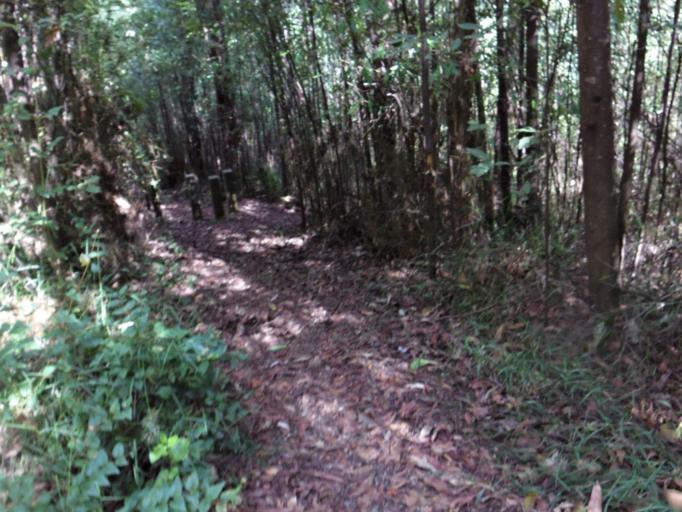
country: AU
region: Victoria
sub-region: Cardinia
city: Bunyip
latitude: -37.9690
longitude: 145.8157
